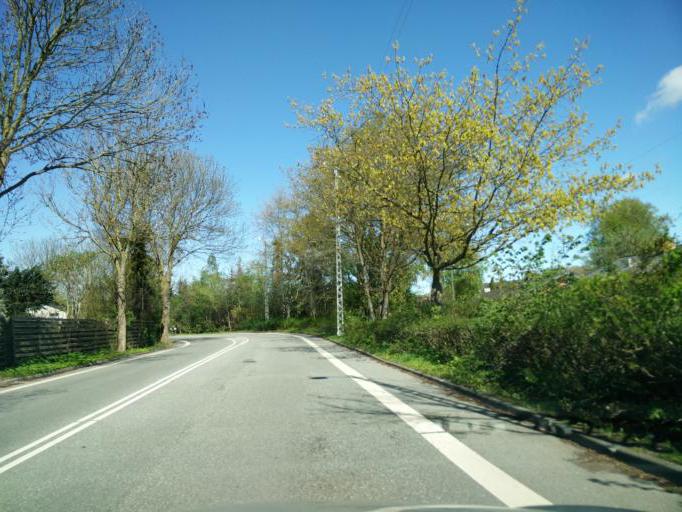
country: DK
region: Capital Region
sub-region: Gribskov Kommune
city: Helsinge
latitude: 56.0218
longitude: 12.2035
